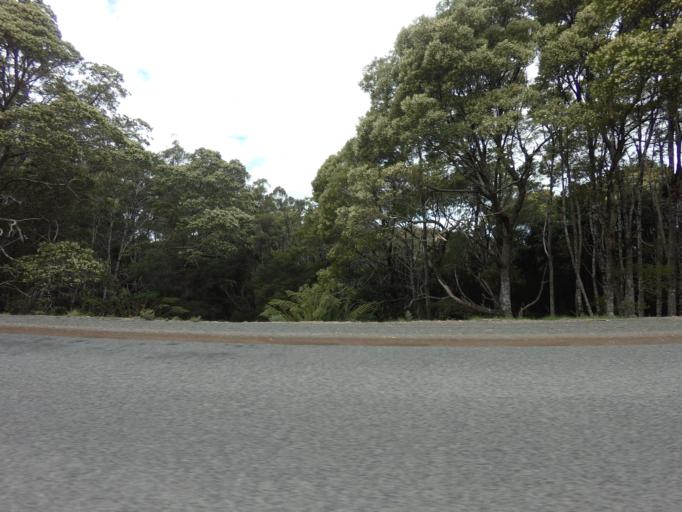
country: AU
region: Tasmania
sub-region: Huon Valley
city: Geeveston
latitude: -43.4285
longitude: 146.9055
